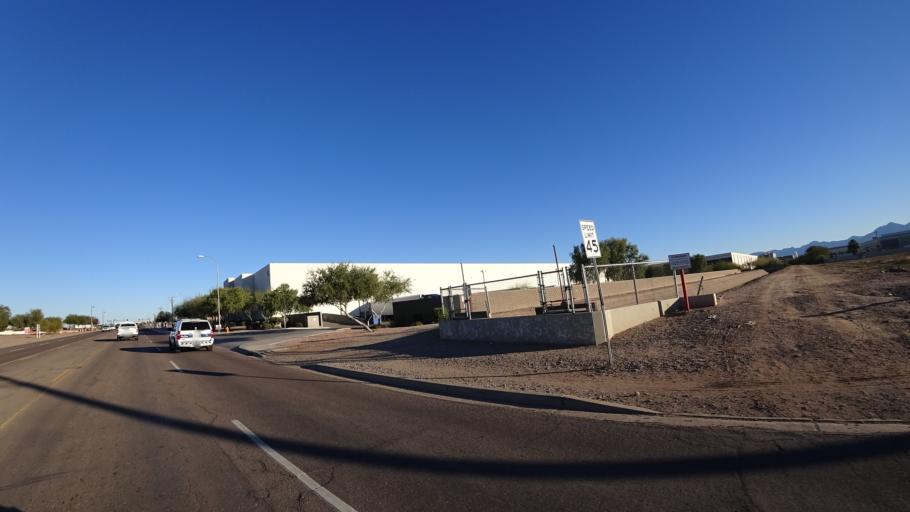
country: US
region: Arizona
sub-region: Maricopa County
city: Tolleson
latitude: 33.4514
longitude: -112.2429
